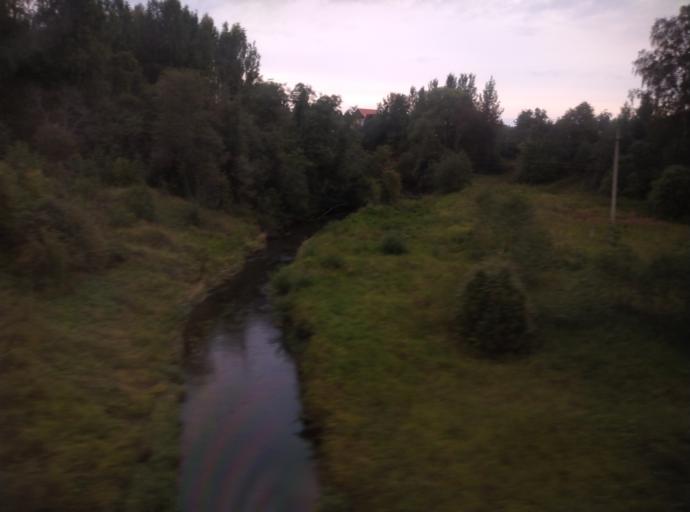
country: RU
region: Jaroslavl
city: Tunoshna
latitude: 57.4942
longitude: 40.1086
